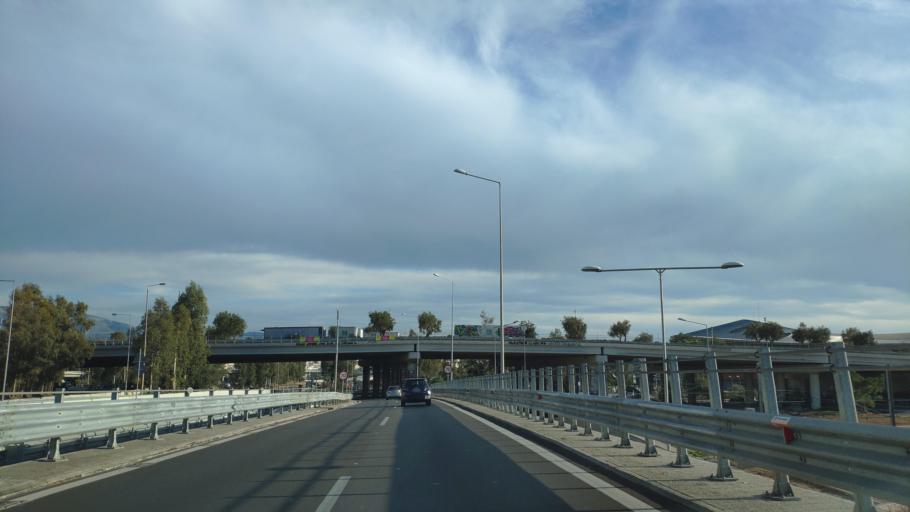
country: GR
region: Attica
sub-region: Nomarchia Athinas
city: Palaio Faliro
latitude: 37.9353
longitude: 23.6923
